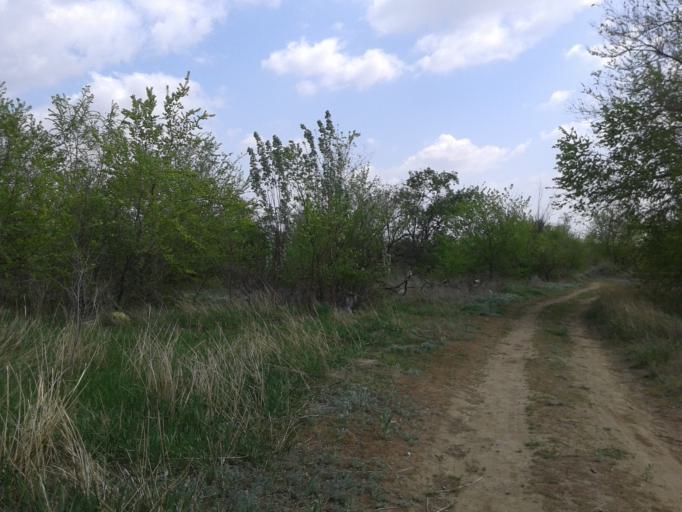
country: RU
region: Volgograd
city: Volgograd
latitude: 48.6427
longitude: 44.4346
